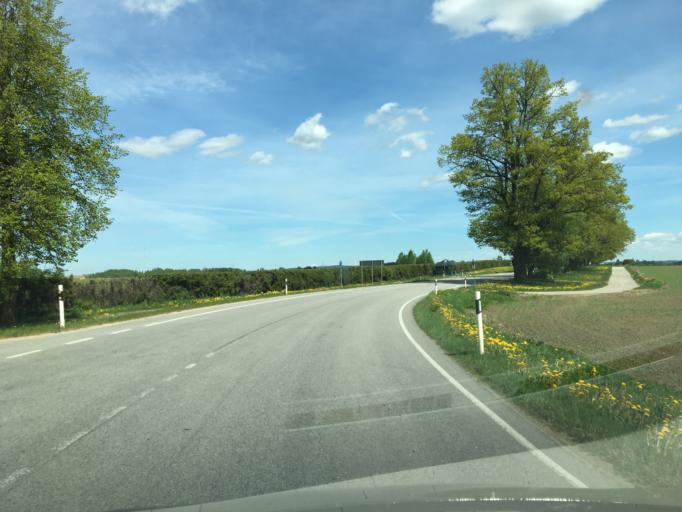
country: EE
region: Vorumaa
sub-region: Antsla vald
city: Vana-Antsla
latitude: 57.9040
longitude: 26.2859
